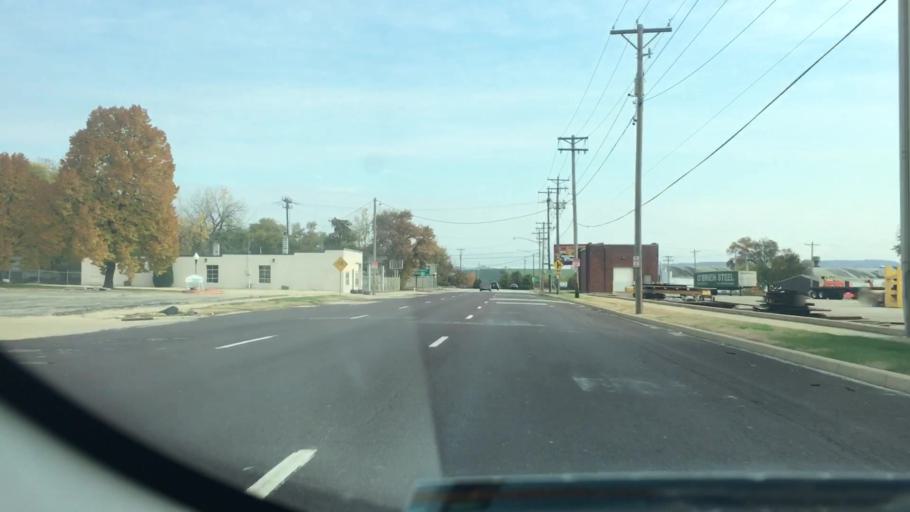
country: US
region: Illinois
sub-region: Peoria County
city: North Peoria
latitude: 40.7054
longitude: -89.5680
